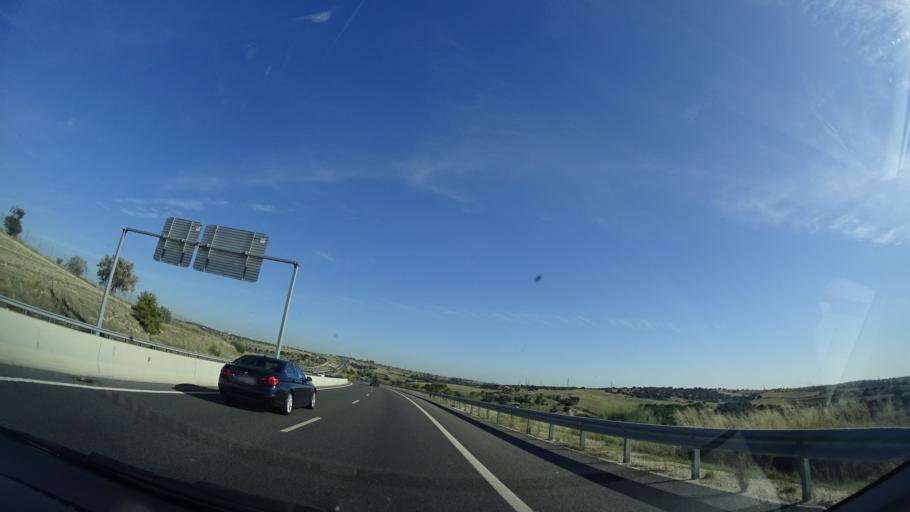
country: ES
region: Madrid
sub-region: Provincia de Madrid
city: Las Rozas de Madrid
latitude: 40.4807
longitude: -3.9183
